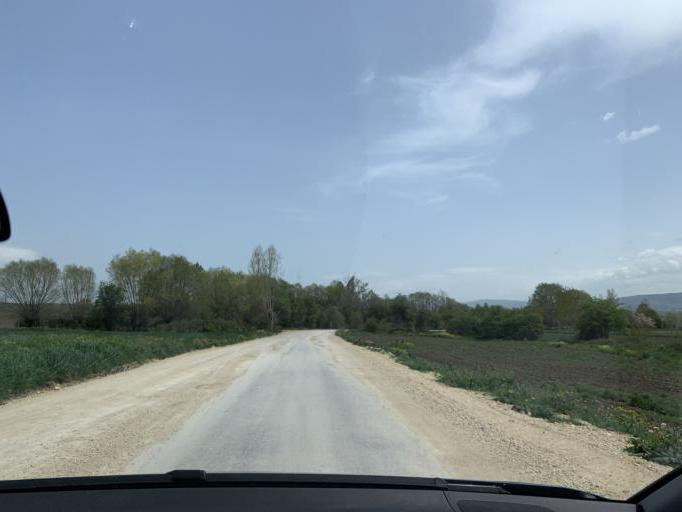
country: TR
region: Bolu
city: Bolu
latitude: 40.7603
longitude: 31.6947
